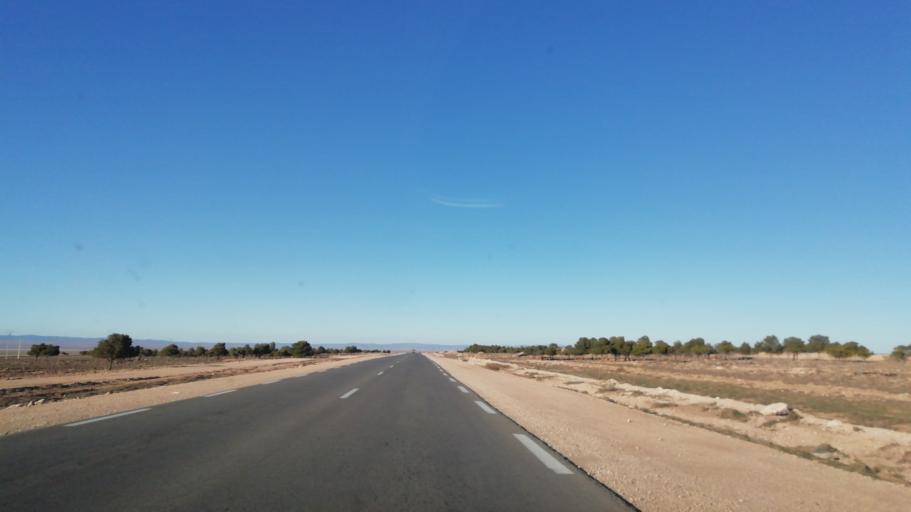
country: DZ
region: Tlemcen
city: Sebdou
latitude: 34.2840
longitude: -1.2594
